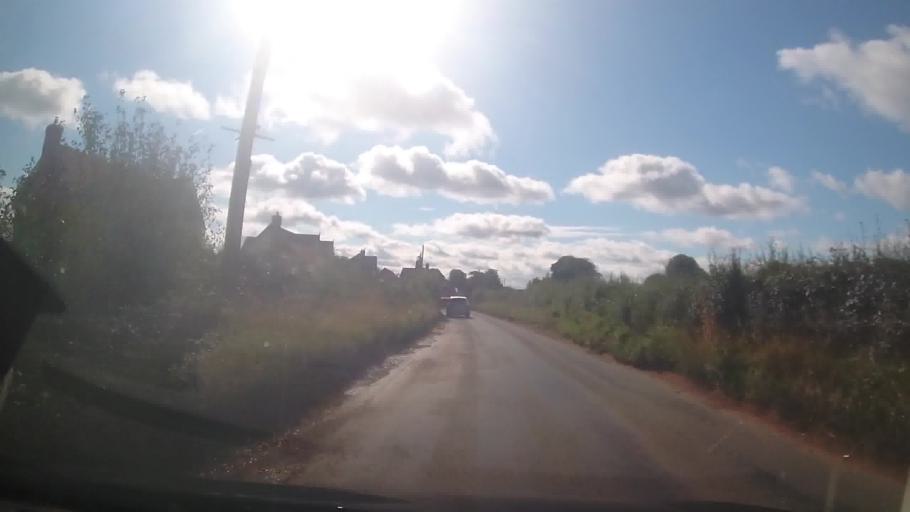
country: GB
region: England
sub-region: Shropshire
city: Ford
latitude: 52.7377
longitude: -2.8463
